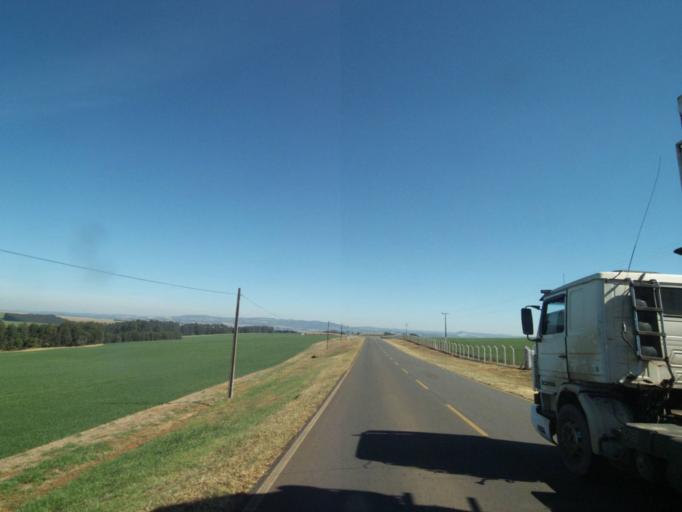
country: BR
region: Parana
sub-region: Tibagi
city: Tibagi
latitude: -24.5231
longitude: -50.3597
